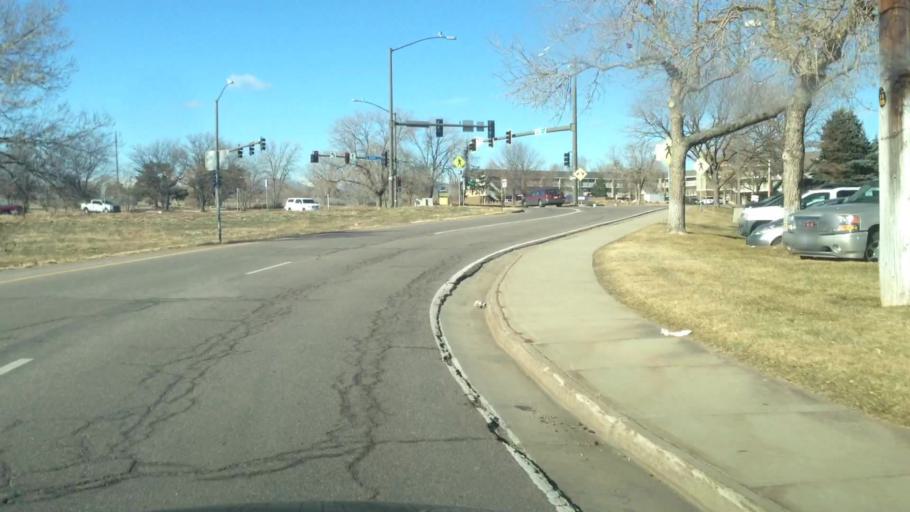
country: US
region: Colorado
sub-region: Jefferson County
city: Lakewood
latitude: 39.7268
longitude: -105.1088
